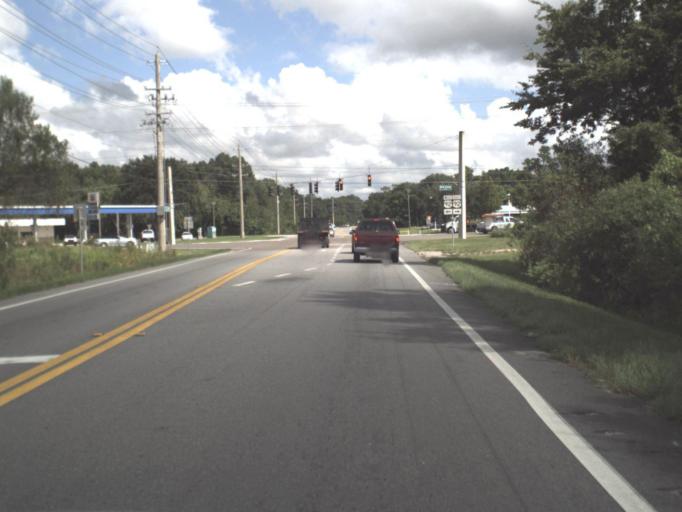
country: US
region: Florida
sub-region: Polk County
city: Winston
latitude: 28.0340
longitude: -82.0192
